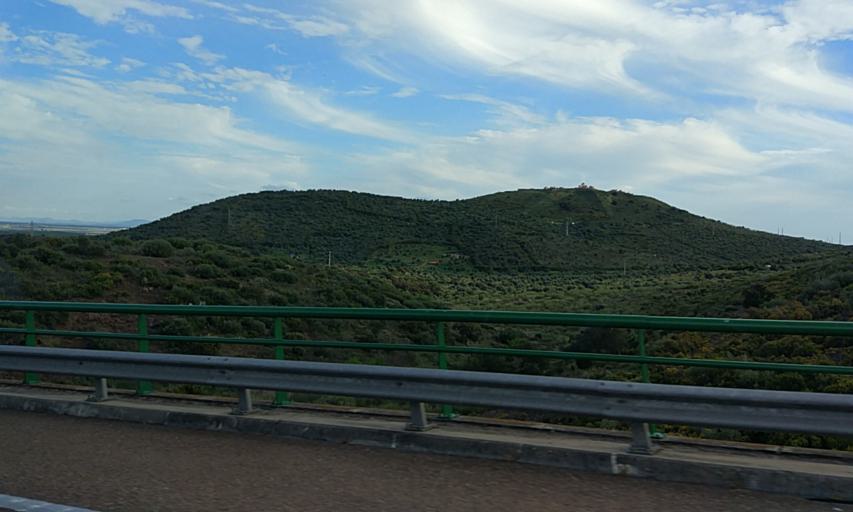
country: PT
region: Portalegre
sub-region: Elvas
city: Elvas
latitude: 38.9086
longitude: -7.1701
